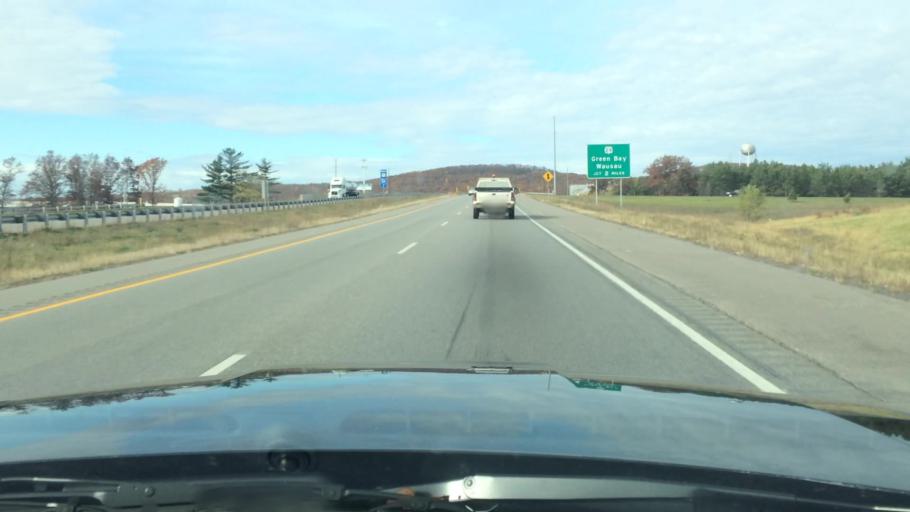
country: US
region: Wisconsin
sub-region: Marathon County
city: Evergreen
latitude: 44.8611
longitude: -89.6391
